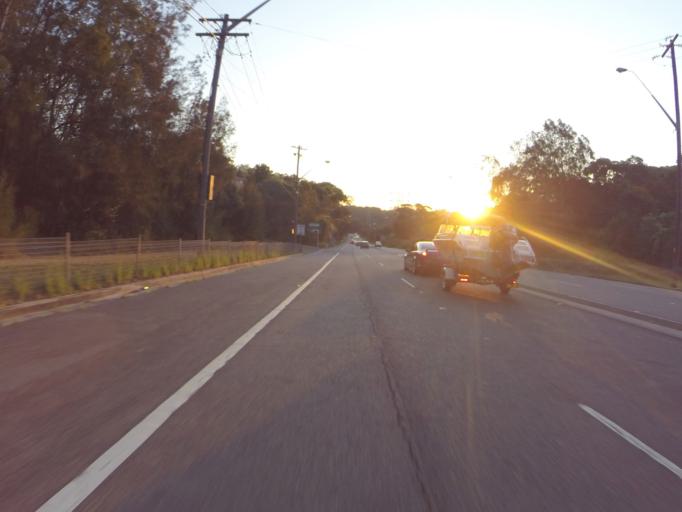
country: AU
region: New South Wales
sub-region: Bankstown
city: Padstow
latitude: -33.9687
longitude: 151.0311
